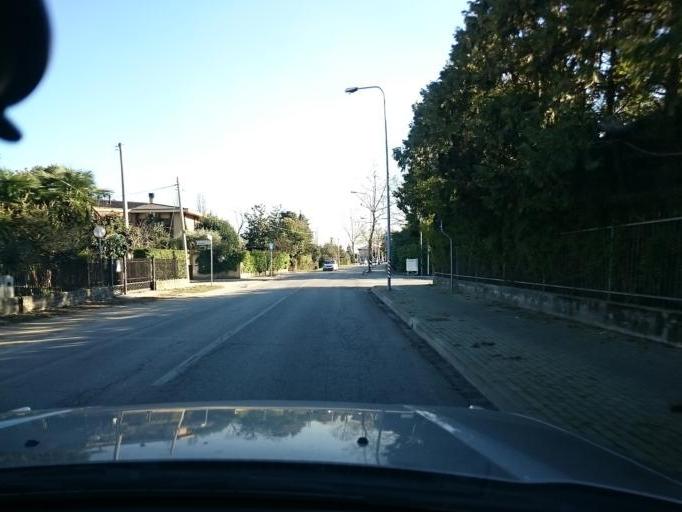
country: IT
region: Veneto
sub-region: Provincia di Padova
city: Montegrotto Terme
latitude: 45.3359
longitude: 11.7934
